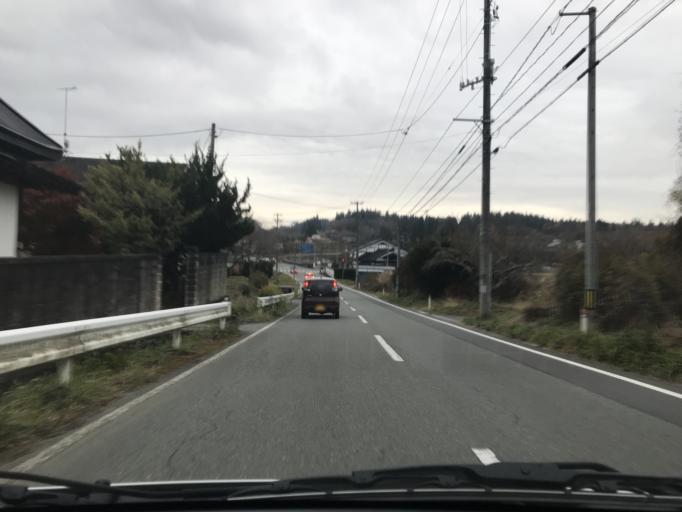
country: JP
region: Iwate
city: Ichinoseki
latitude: 39.0224
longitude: 141.3308
